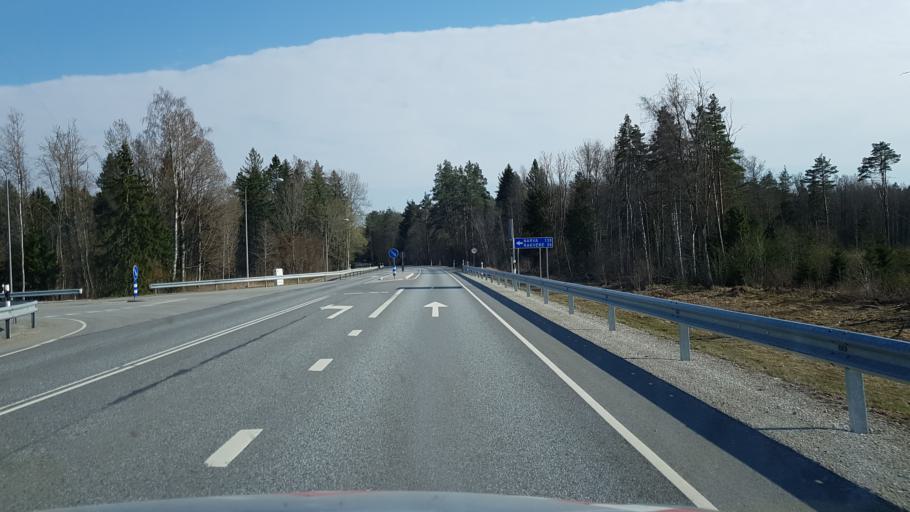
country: EE
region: Laeaene-Virumaa
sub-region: Kadrina vald
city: Kadrina
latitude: 59.4618
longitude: 26.0033
